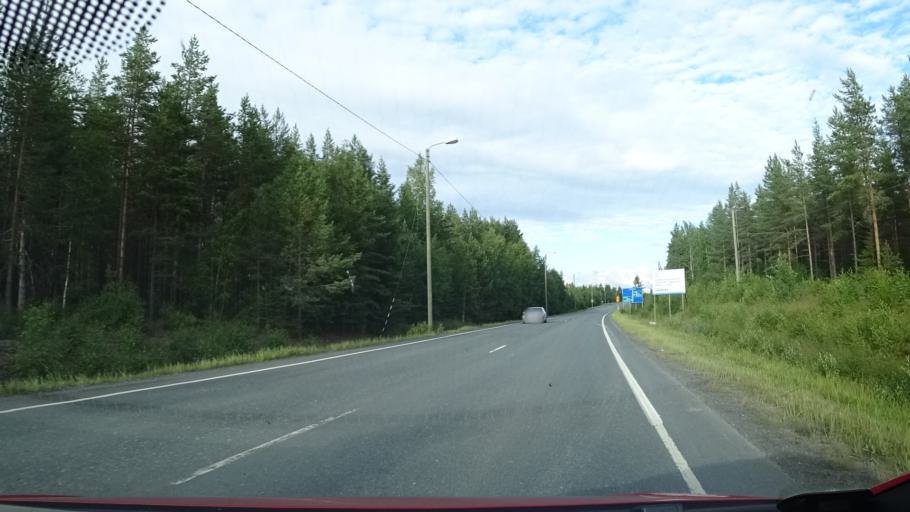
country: FI
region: Northern Ostrobothnia
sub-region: Oulu
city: Haukipudas
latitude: 65.2008
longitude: 25.4137
